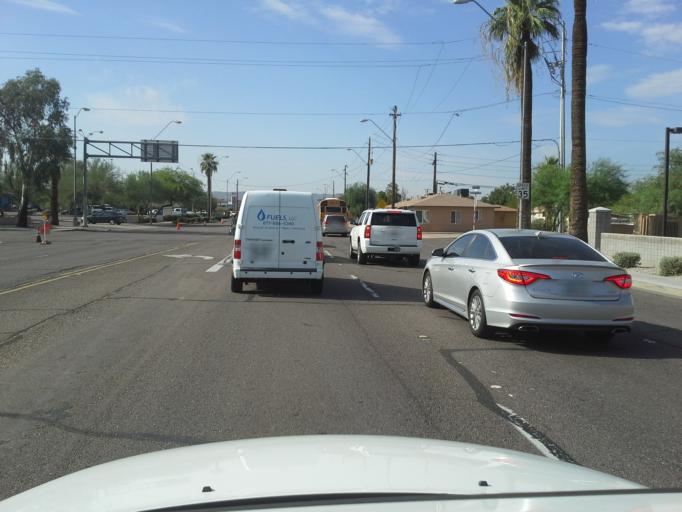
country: US
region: Arizona
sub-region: Maricopa County
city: Phoenix
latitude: 33.4609
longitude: -112.0477
